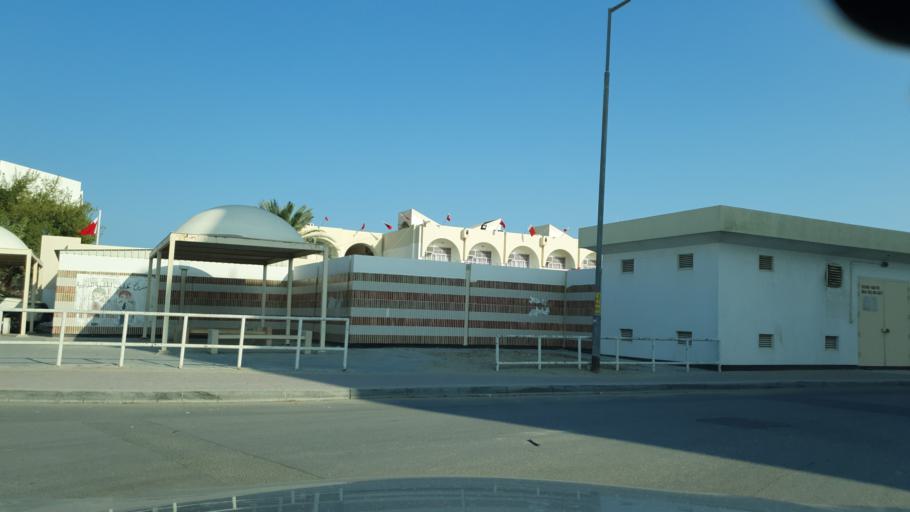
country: BH
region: Manama
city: Jidd Hafs
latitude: 26.2236
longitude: 50.4613
